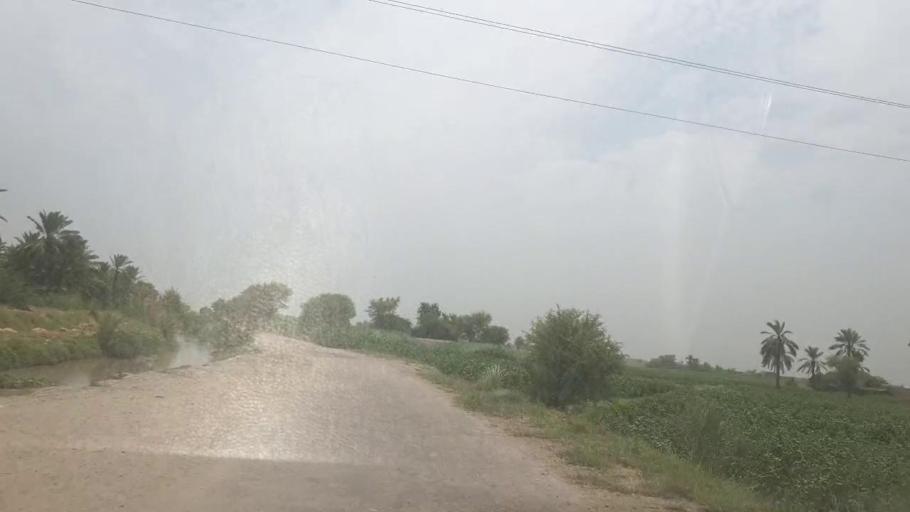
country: PK
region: Sindh
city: Kot Diji
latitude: 27.4273
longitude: 68.6505
